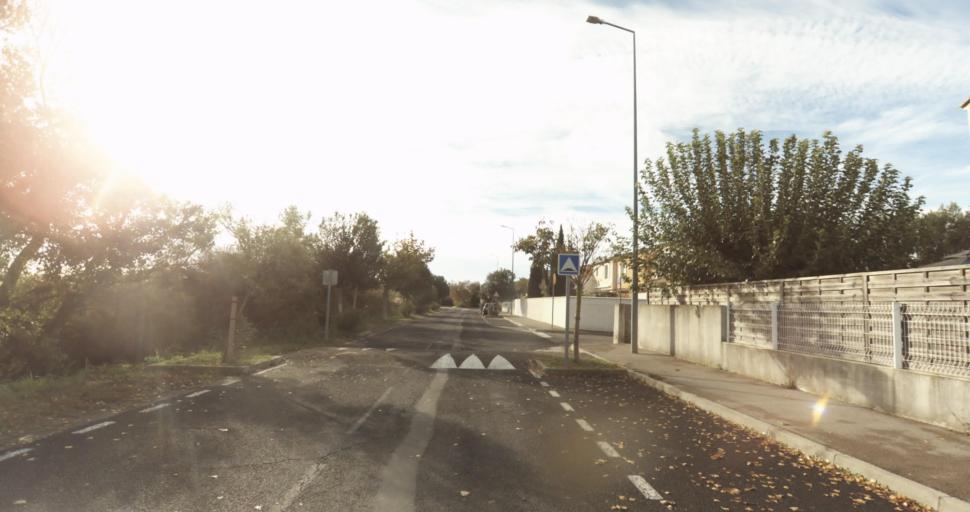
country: FR
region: Languedoc-Roussillon
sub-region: Departement du Gard
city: Aigues-Mortes
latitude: 43.5664
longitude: 4.2073
